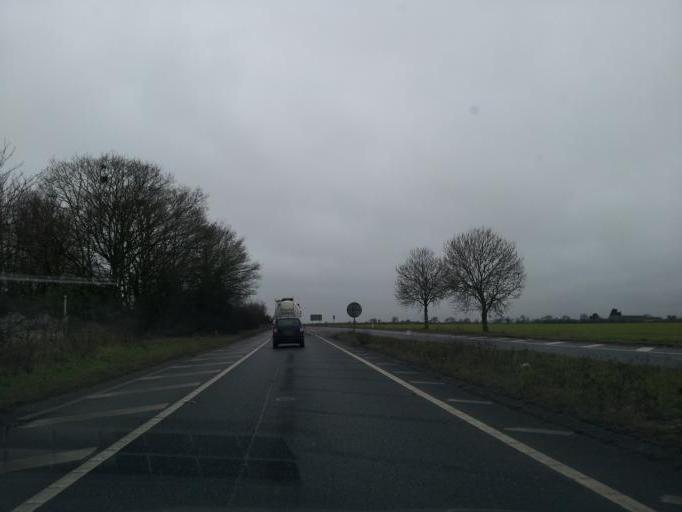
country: GB
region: England
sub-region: Essex
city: Great Bentley
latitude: 51.8958
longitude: 1.0681
